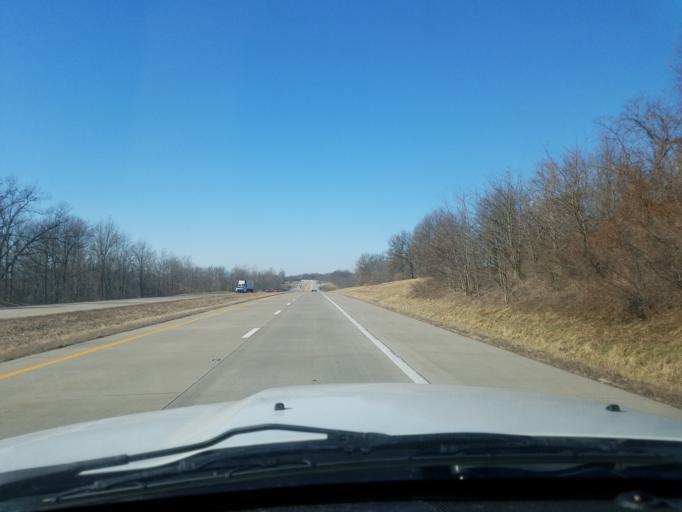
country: US
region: Indiana
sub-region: Warrick County
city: Newburgh
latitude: 37.7614
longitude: -87.4175
